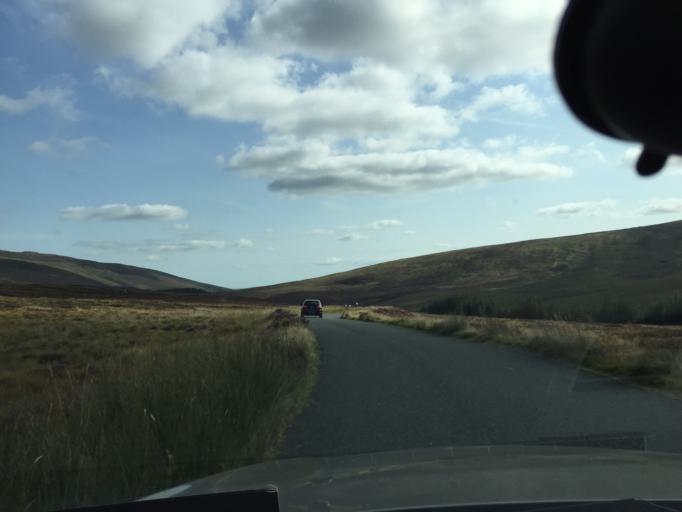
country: IE
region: Leinster
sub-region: Wicklow
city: Rathdrum
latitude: 53.0765
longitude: -6.3541
